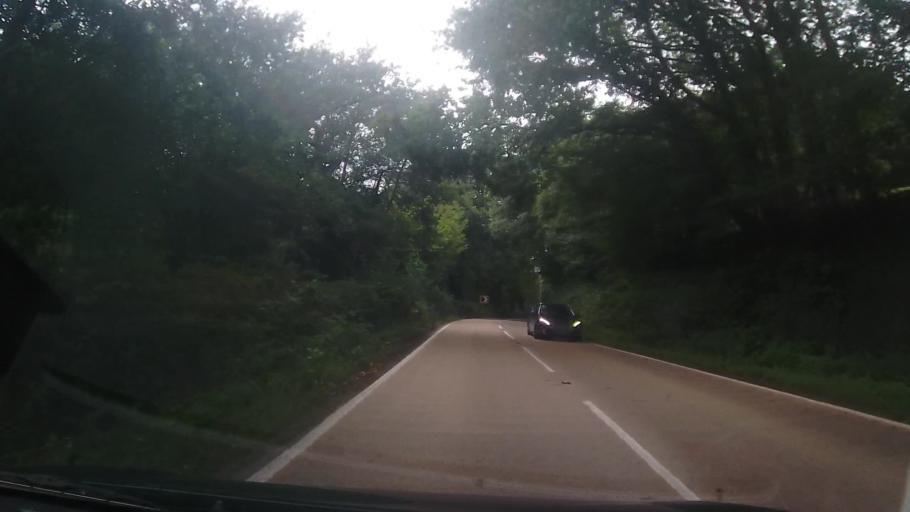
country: GB
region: Wales
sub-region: Sir Powys
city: Machynlleth
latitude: 52.5636
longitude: -3.9124
